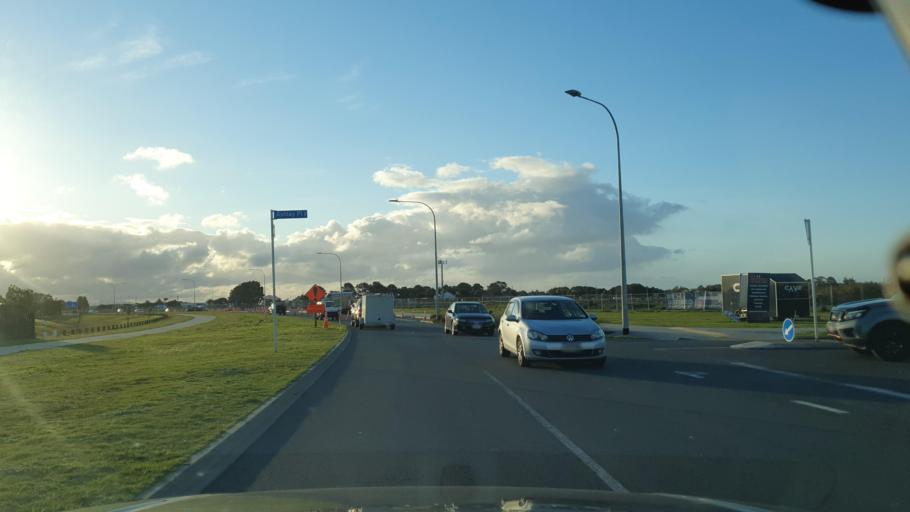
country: NZ
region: Bay of Plenty
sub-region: Western Bay of Plenty District
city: Maketu
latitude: -37.7157
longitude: 176.3138
